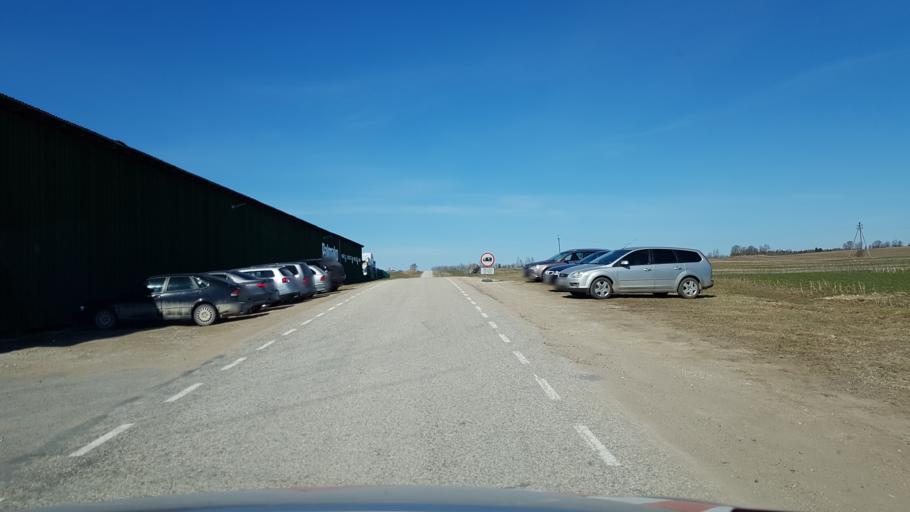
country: EE
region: Laeaene-Virumaa
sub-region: Vinni vald
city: Vinni
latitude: 59.0714
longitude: 26.5546
